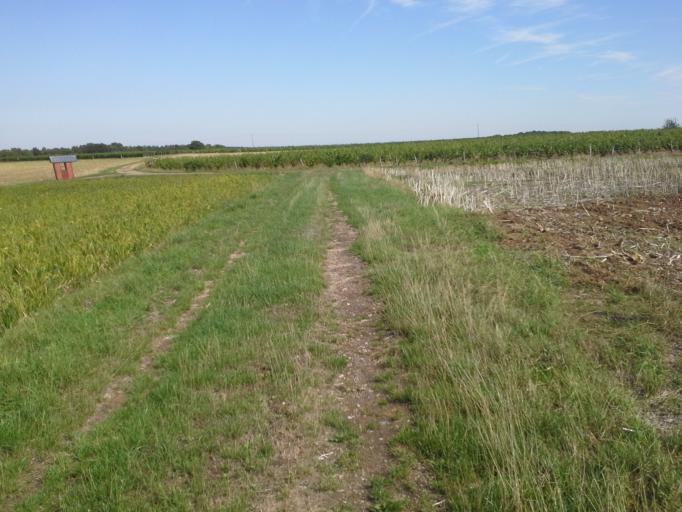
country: FR
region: Centre
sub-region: Departement du Loir-et-Cher
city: Villiers-sur-Loir
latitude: 47.8188
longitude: 0.9815
